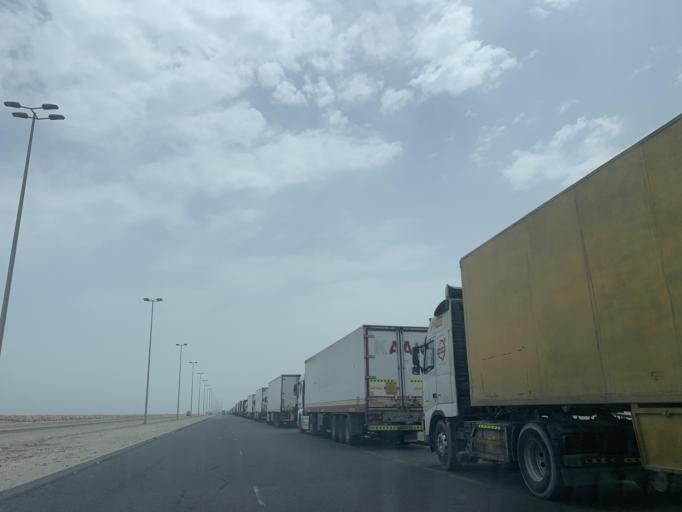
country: BH
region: Muharraq
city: Al Hadd
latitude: 26.2079
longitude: 50.7056
